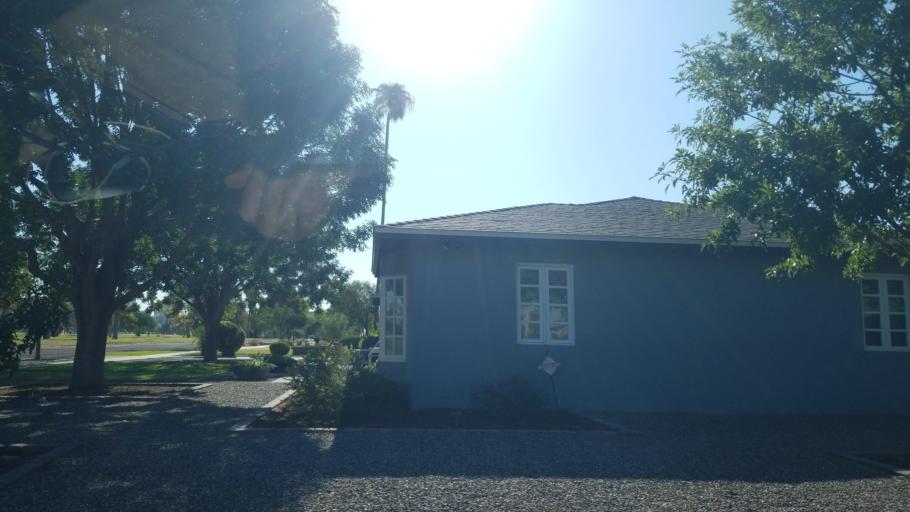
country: US
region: Arizona
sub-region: Maricopa County
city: Phoenix
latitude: 33.4767
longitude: -112.0957
